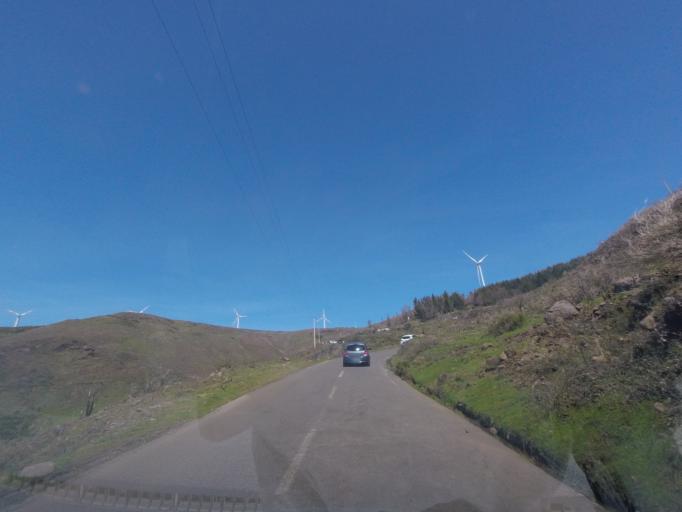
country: PT
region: Madeira
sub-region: Calheta
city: Arco da Calheta
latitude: 32.7382
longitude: -17.1032
